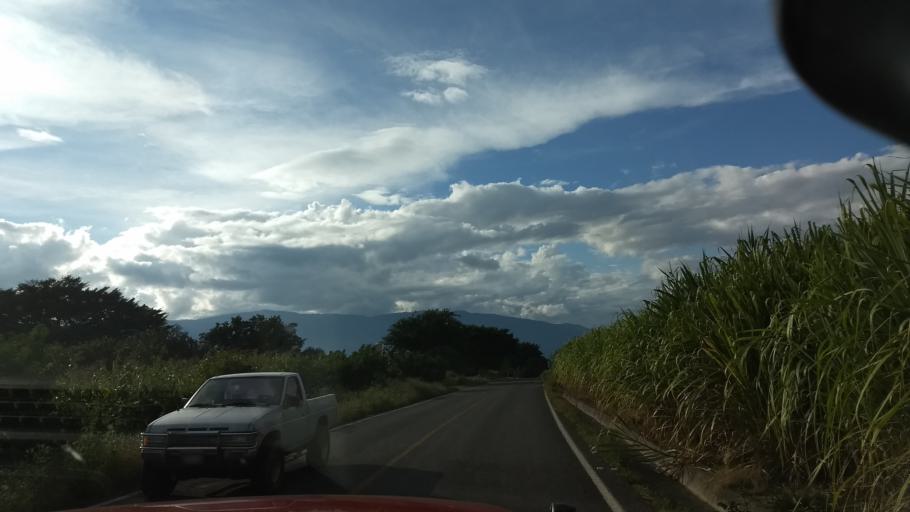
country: MX
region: Colima
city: Suchitlan
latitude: 19.4670
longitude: -103.7619
